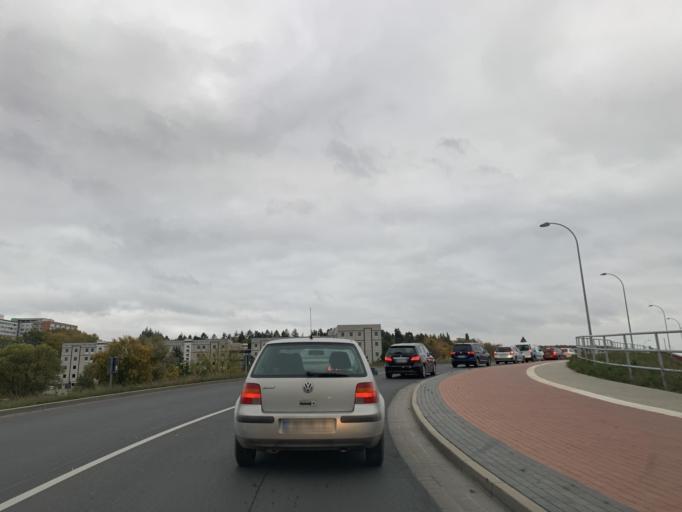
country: DE
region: Mecklenburg-Vorpommern
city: Neubrandenburg
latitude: 53.5602
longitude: 13.2853
